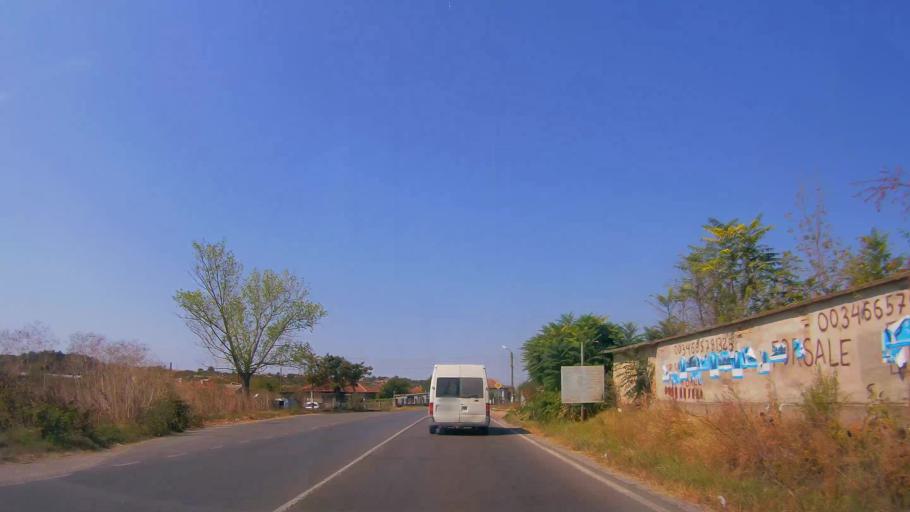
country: BG
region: Razgrad
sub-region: Obshtina Tsar Kaloyan
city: Tsar Kaloyan
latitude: 43.6001
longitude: 26.2462
